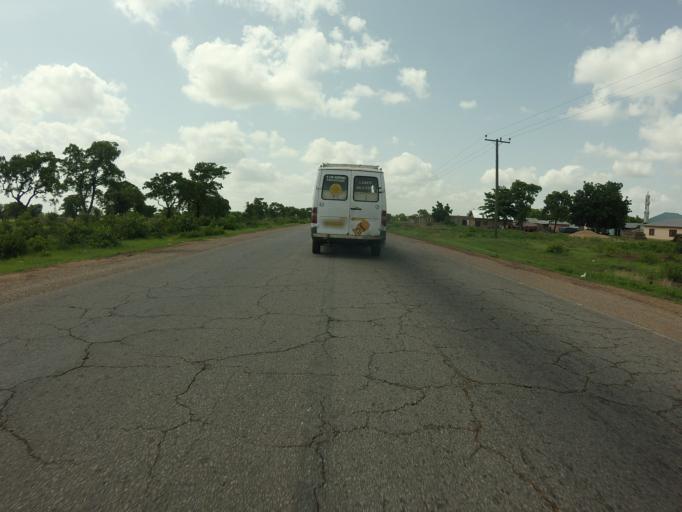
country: GH
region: Northern
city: Savelugu
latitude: 9.5882
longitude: -0.8328
